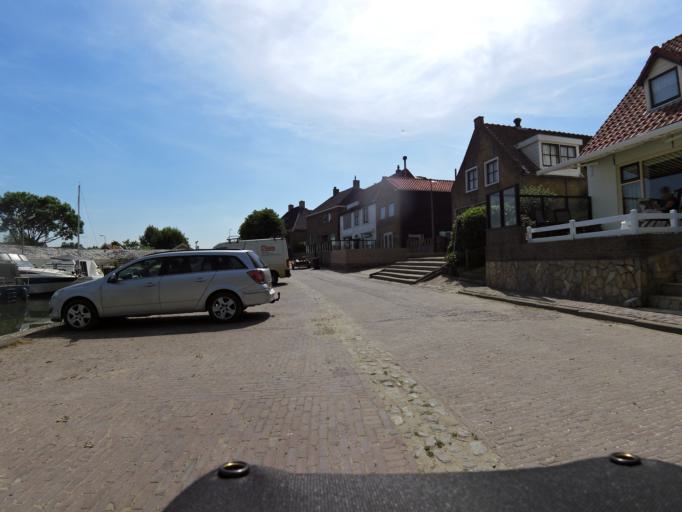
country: NL
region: South Holland
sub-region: Gemeente Spijkenisse
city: Spijkenisse
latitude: 51.7970
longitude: 4.2731
